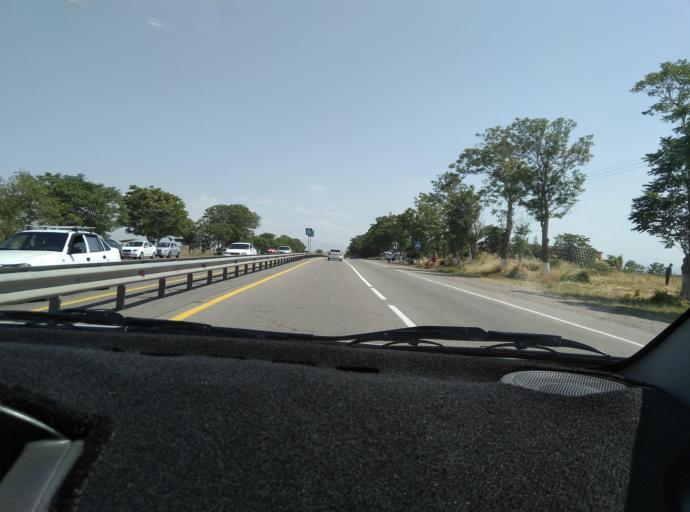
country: UZ
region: Toshkent
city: Ohangaron
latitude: 40.9845
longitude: 69.5378
